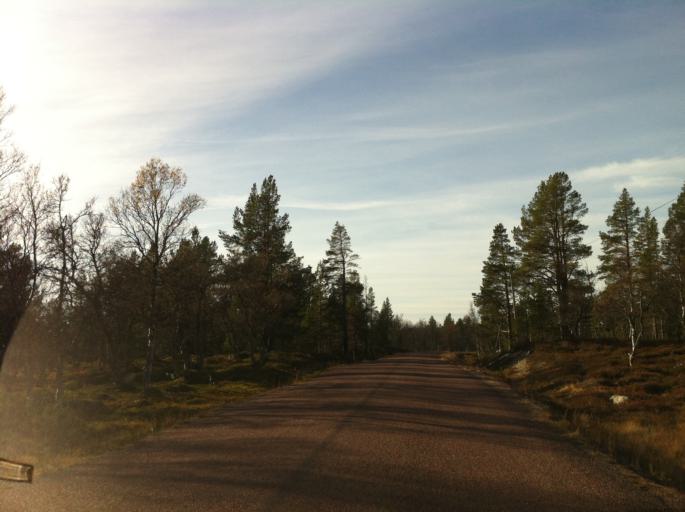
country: NO
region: Hedmark
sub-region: Engerdal
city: Engerdal
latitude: 62.0711
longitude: 12.2051
